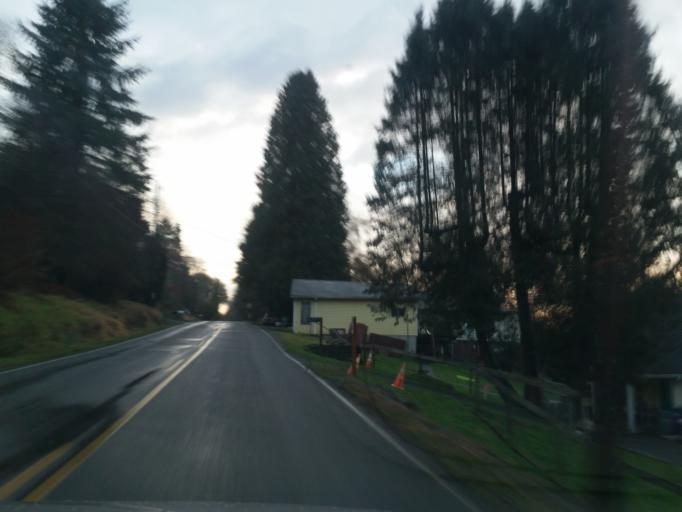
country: US
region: Washington
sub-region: Snohomish County
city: Cathcart
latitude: 47.8491
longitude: -122.0928
